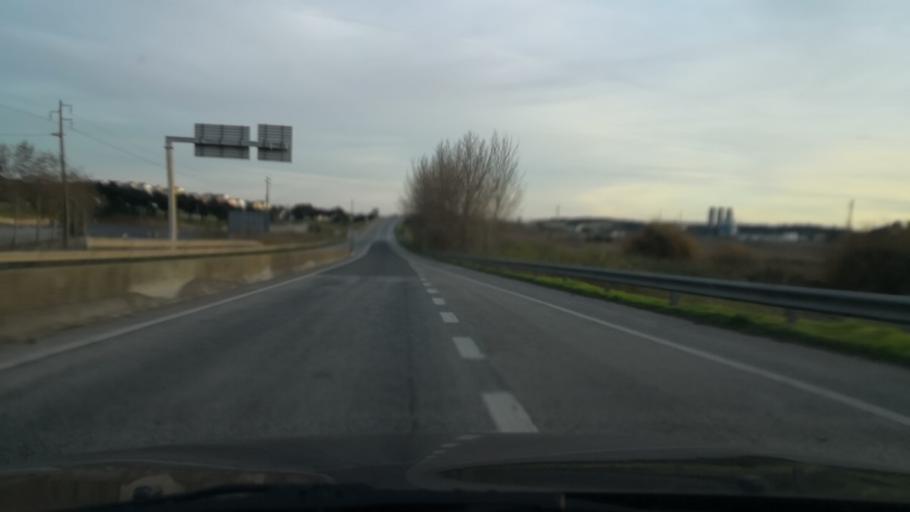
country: PT
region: Setubal
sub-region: Setubal
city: Setubal
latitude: 38.5218
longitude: -8.8421
